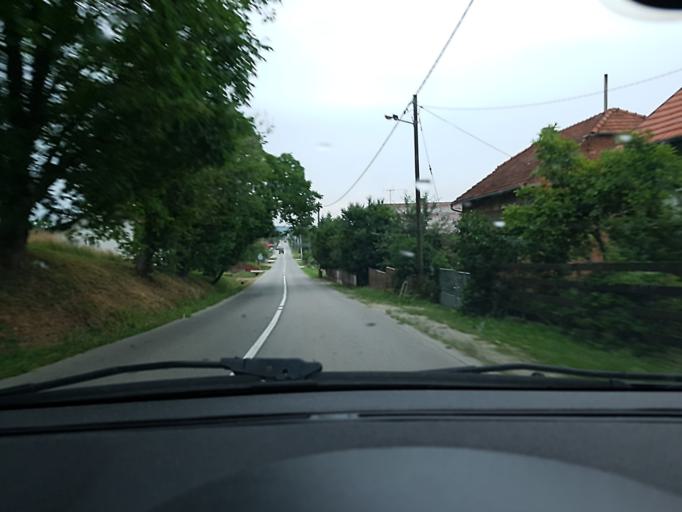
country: HR
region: Zagrebacka
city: Pojatno
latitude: 45.9268
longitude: 15.8154
